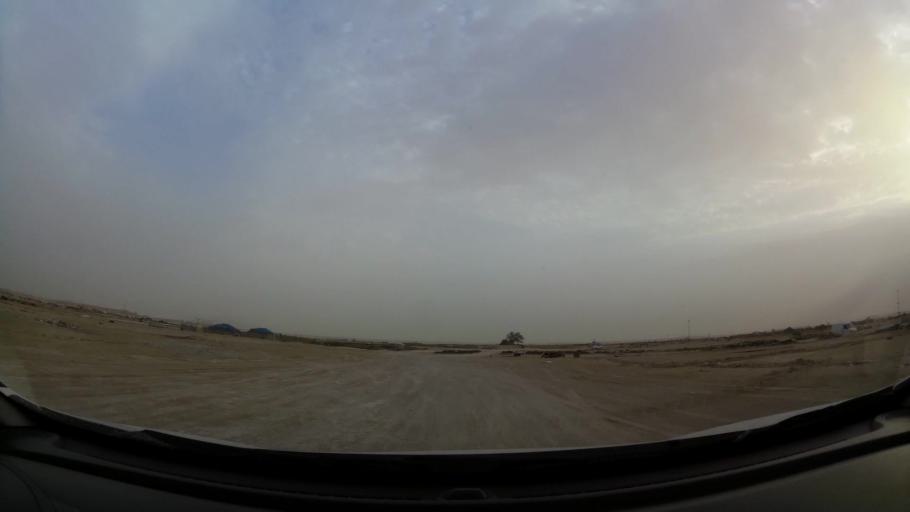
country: BH
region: Central Governorate
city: Dar Kulayb
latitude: 25.9979
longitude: 50.5845
